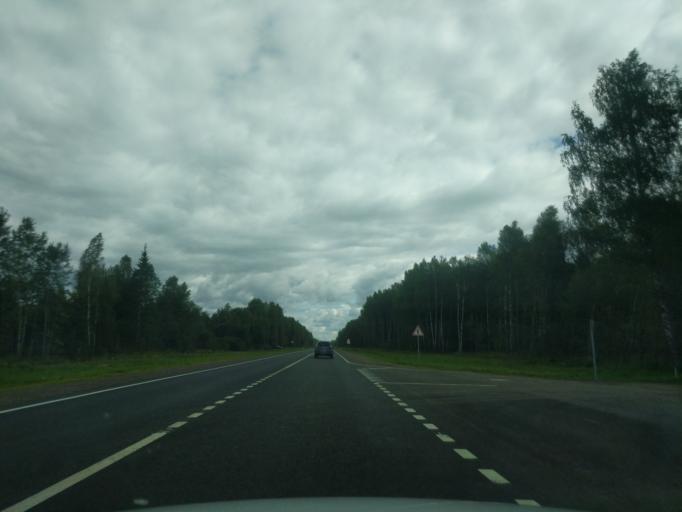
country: RU
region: Jaroslavl
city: Tunoshna
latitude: 57.5542
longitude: 40.2001
